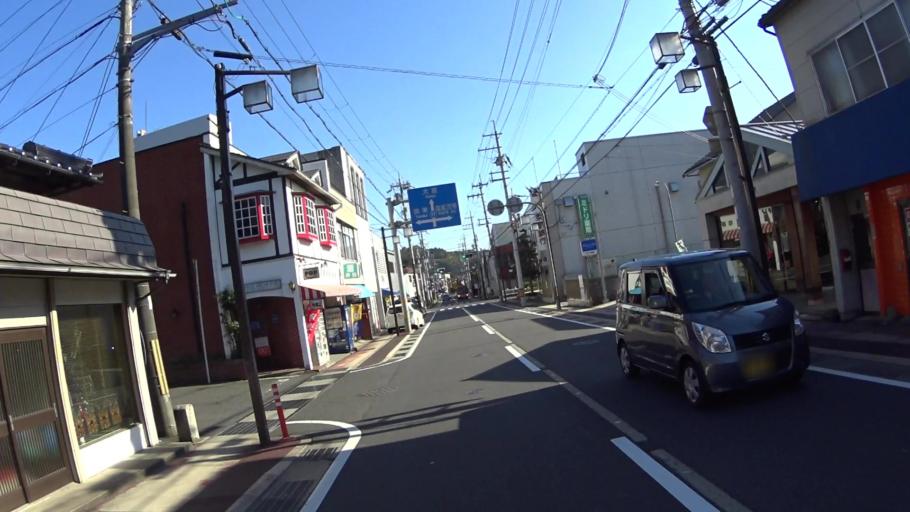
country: JP
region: Kyoto
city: Miyazu
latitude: 35.6257
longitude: 135.0575
